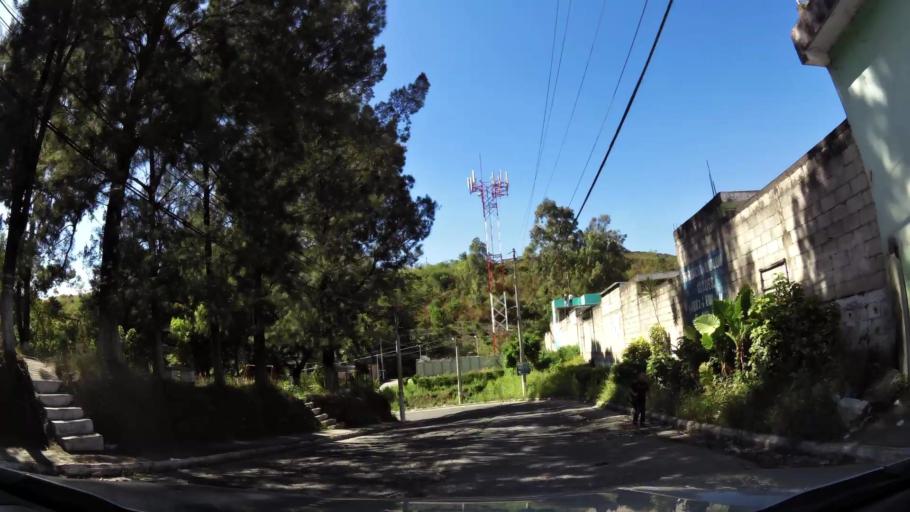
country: GT
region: Guatemala
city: Petapa
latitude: 14.4935
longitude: -90.5483
